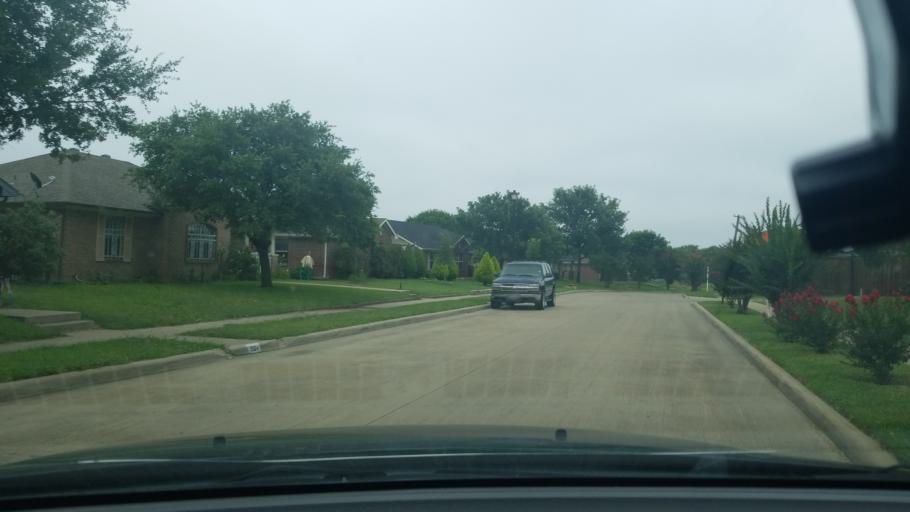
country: US
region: Texas
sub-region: Dallas County
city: Balch Springs
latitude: 32.7561
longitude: -96.6878
